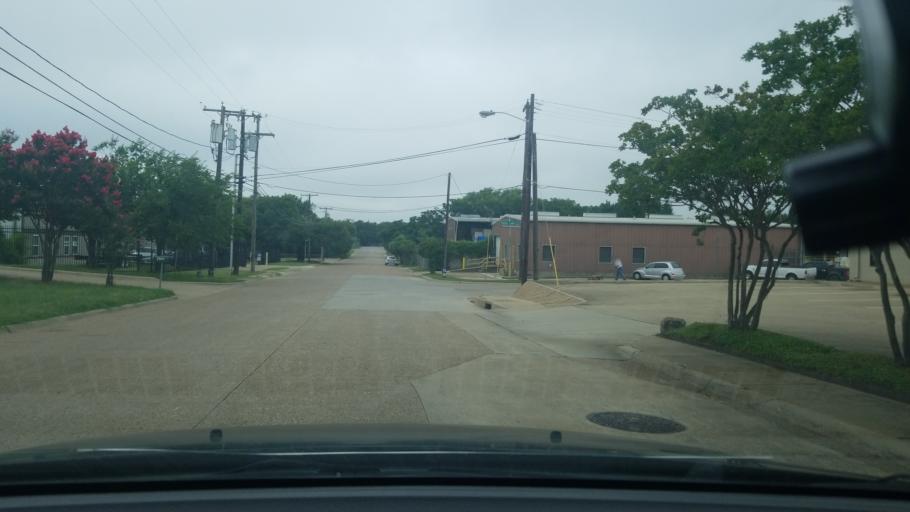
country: US
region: Texas
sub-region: Dallas County
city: Balch Springs
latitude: 32.7732
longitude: -96.6854
